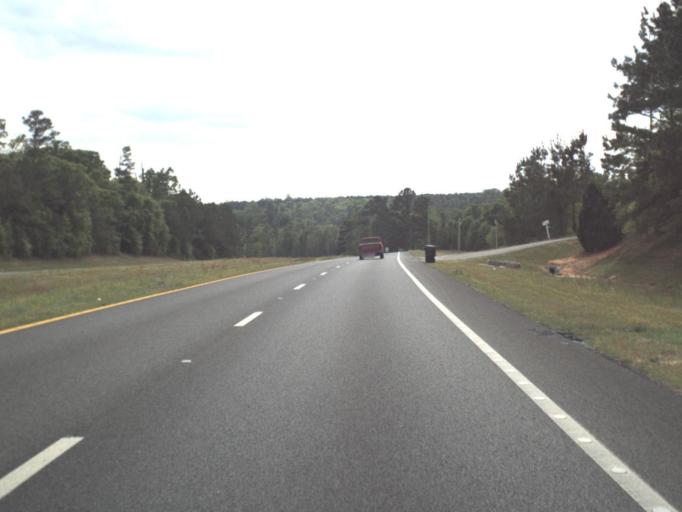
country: US
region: Florida
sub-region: Escambia County
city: Century
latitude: 30.9240
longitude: -87.3101
